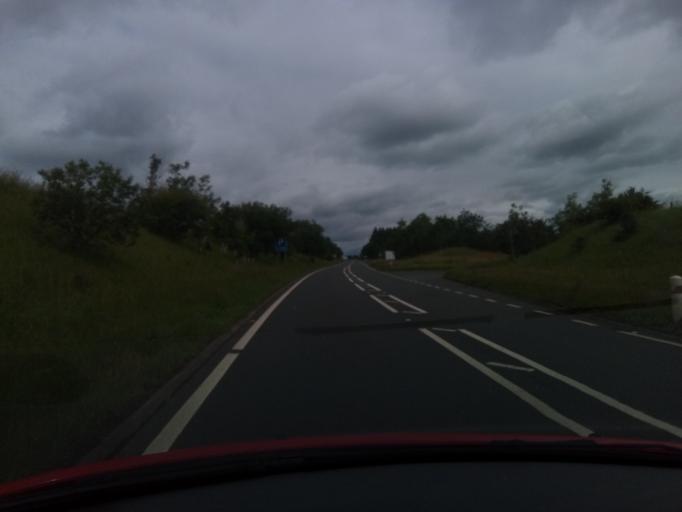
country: GB
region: Scotland
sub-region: The Scottish Borders
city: Hawick
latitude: 55.4551
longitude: -2.7799
